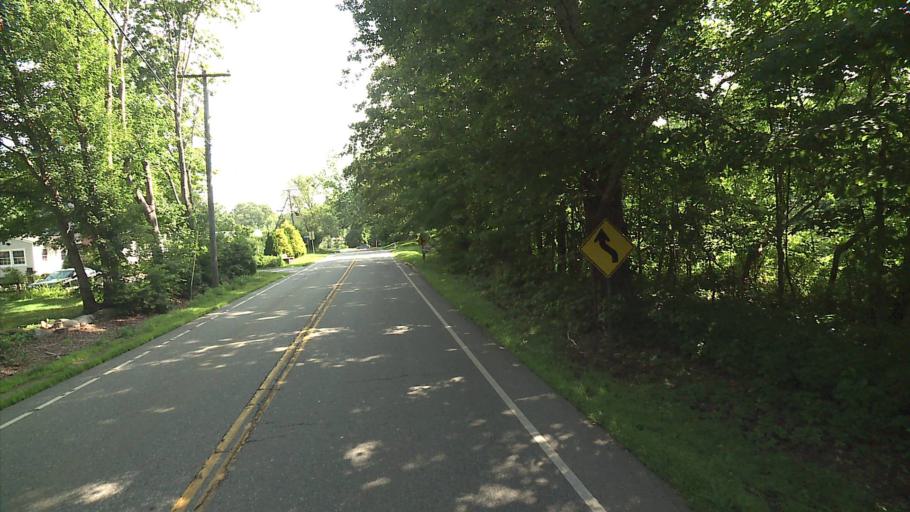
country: US
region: Connecticut
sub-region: Middlesex County
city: Clinton
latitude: 41.2860
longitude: -72.4933
